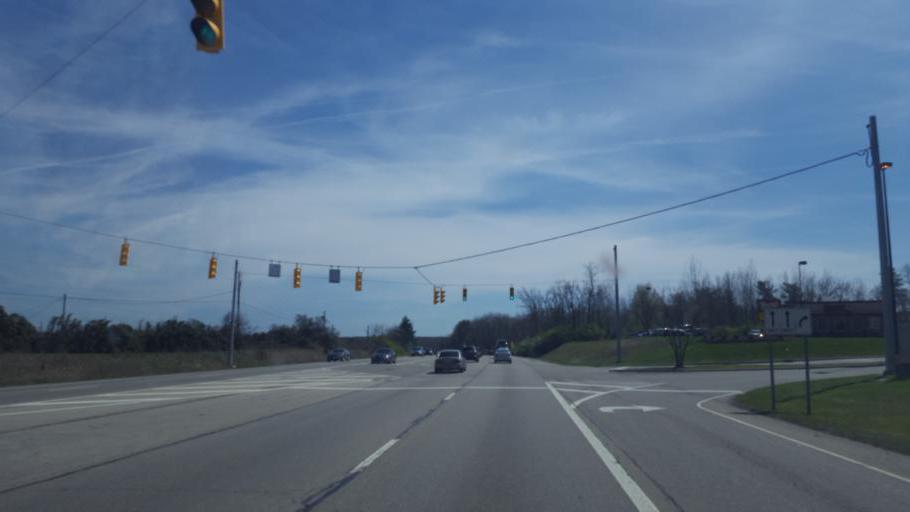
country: US
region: Ohio
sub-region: Delaware County
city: Delaware
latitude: 40.2655
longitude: -83.0697
